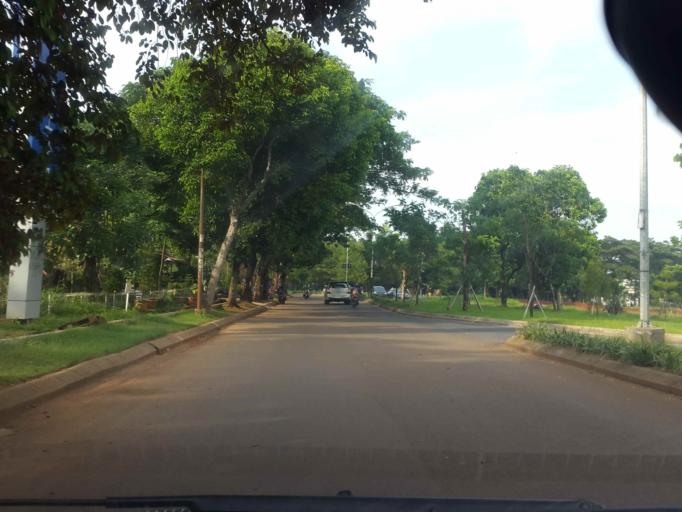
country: ID
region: West Java
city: Ciputat
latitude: -6.2675
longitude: 106.6883
